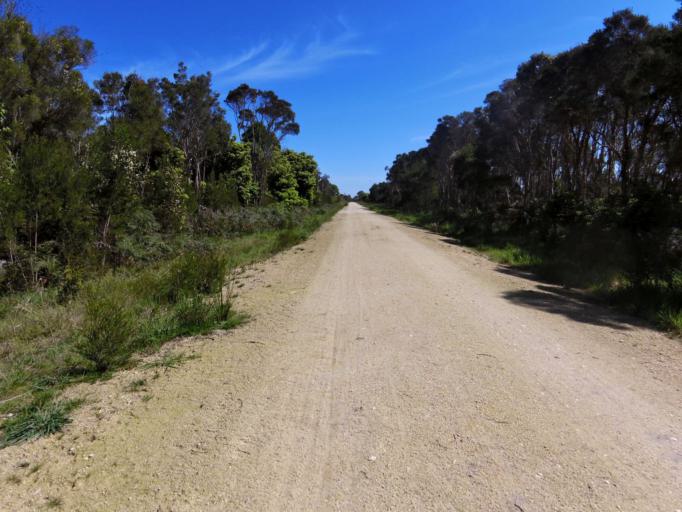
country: AU
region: Victoria
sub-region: Latrobe
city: Morwell
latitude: -38.6691
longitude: 146.4227
